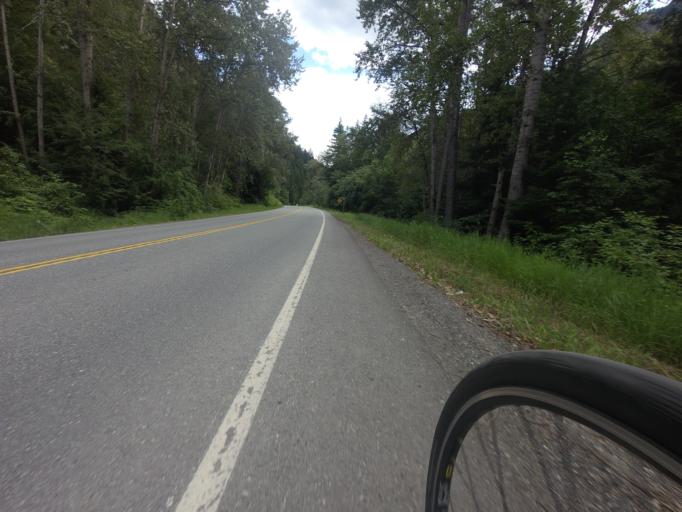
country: CA
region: British Columbia
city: Lillooet
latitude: 50.6178
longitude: -122.1036
